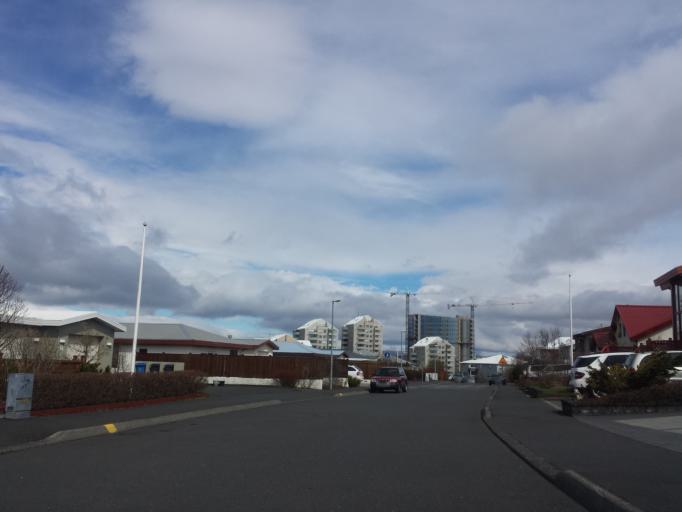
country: IS
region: Capital Region
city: Kopavogur
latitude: 64.1006
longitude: -21.8966
